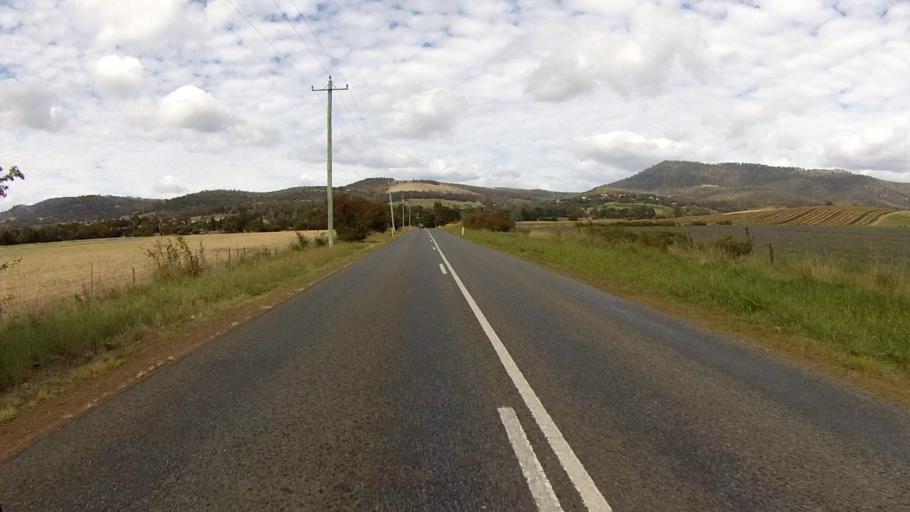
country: AU
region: Tasmania
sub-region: Clarence
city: Cambridge
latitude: -42.7563
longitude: 147.4054
